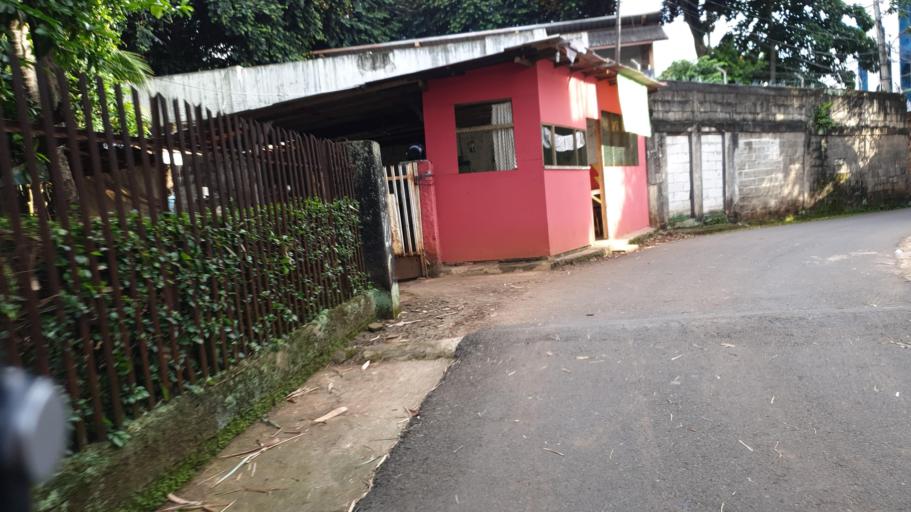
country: ID
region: Banten
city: South Tangerang
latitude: -6.2911
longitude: 106.7882
